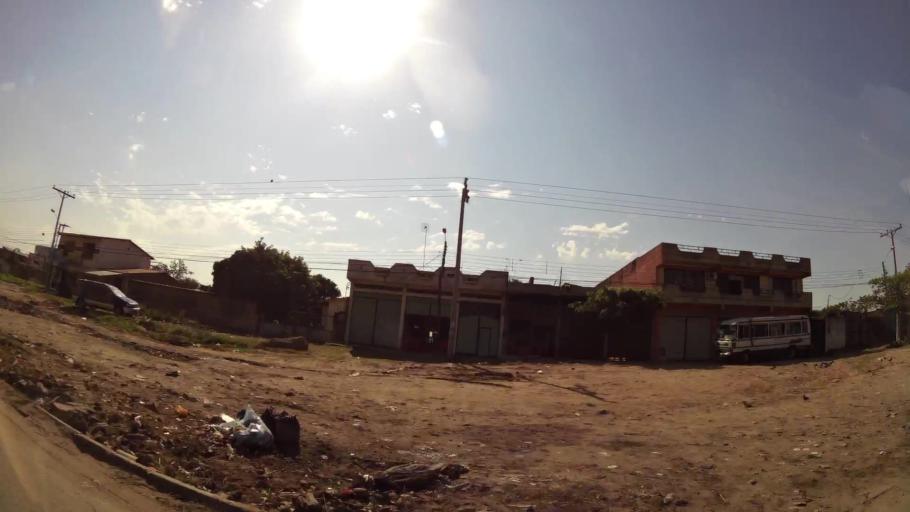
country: BO
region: Santa Cruz
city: Santa Cruz de la Sierra
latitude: -17.8235
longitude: -63.1291
